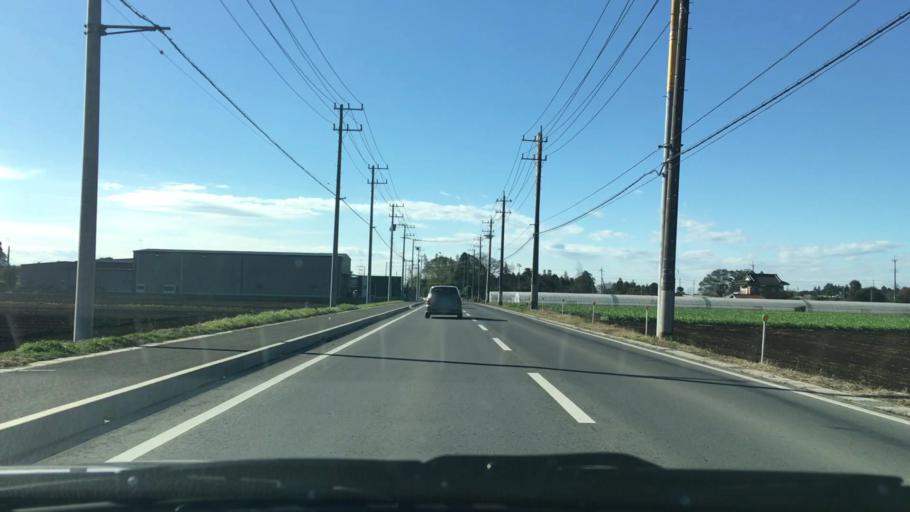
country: JP
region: Chiba
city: Sawara
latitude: 35.8357
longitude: 140.5390
